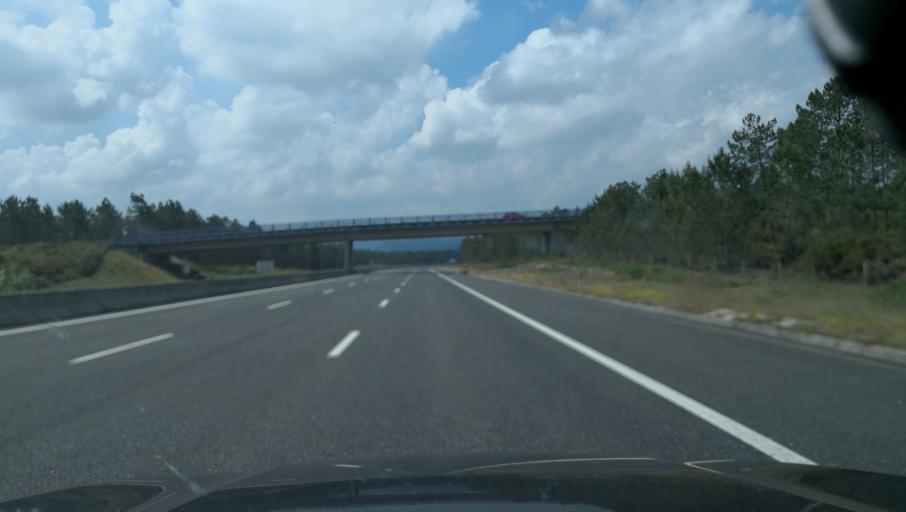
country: PT
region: Leiria
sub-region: Alcobaca
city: Alcobaca
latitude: 39.6013
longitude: -9.0008
